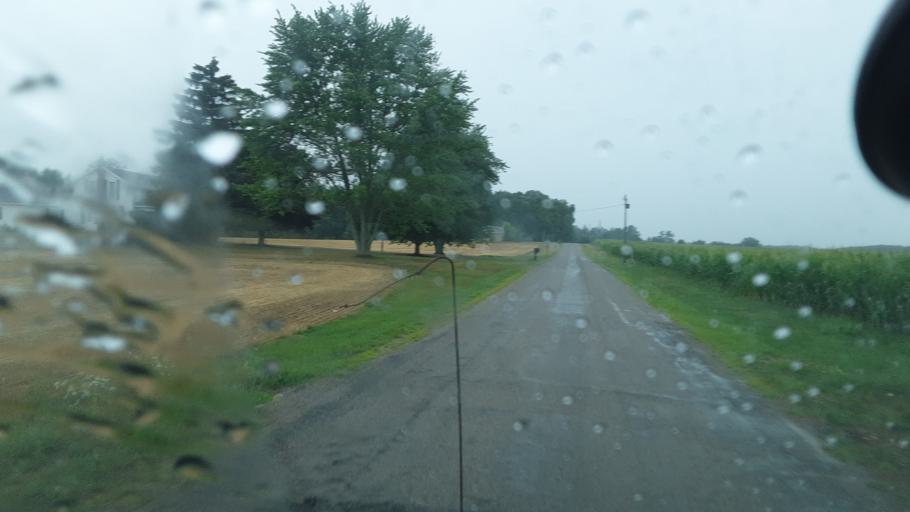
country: US
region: Ohio
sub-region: Williams County
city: Edgerton
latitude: 41.4262
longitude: -84.8048
